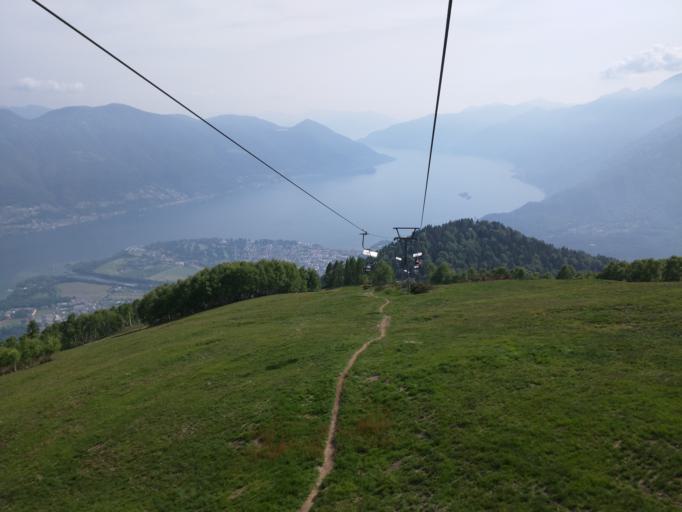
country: CH
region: Ticino
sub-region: Locarno District
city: Locarno
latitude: 46.1982
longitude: 8.7875
